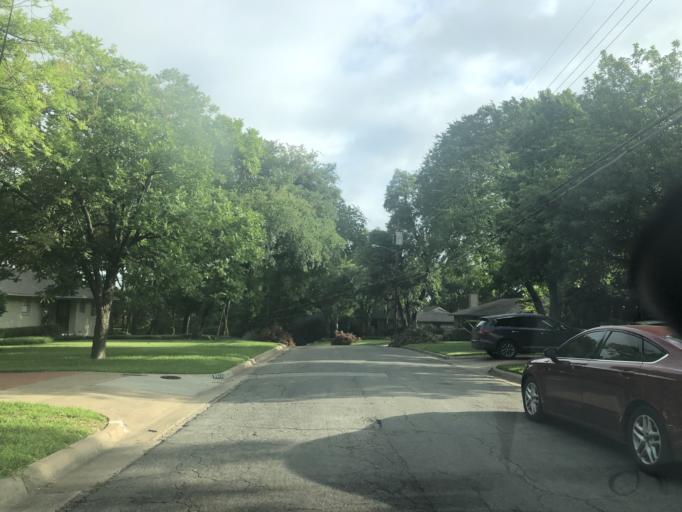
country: US
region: Texas
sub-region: Dallas County
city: University Park
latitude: 32.8563
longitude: -96.8410
